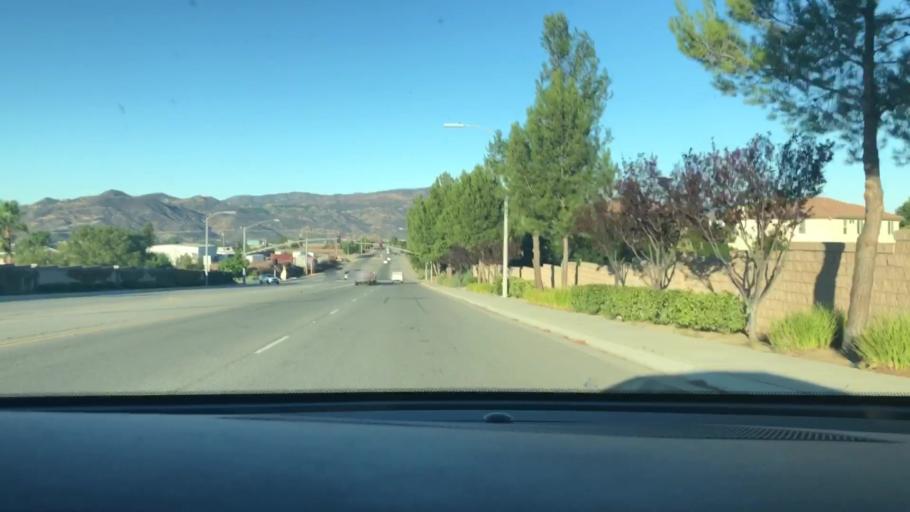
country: US
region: California
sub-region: Riverside County
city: Murrieta
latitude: 33.5979
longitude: -117.2223
